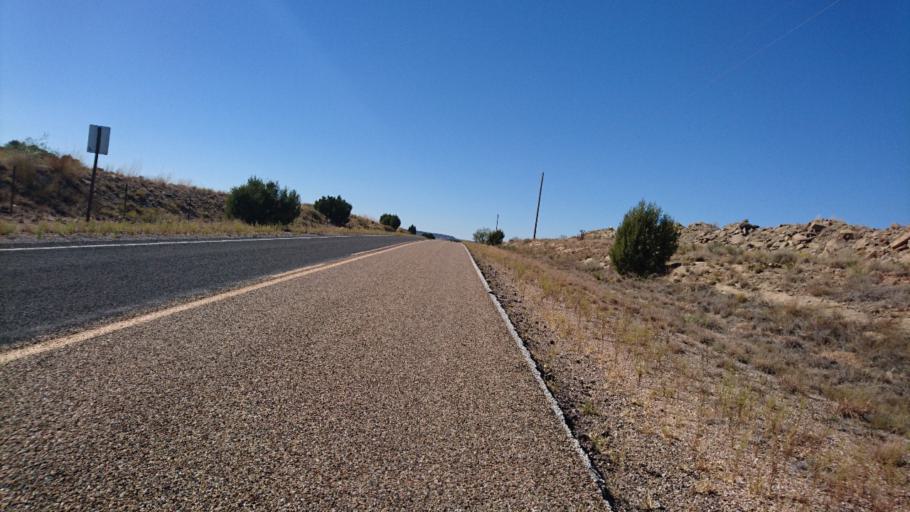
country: US
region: New Mexico
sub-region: Quay County
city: Tucumcari
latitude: 35.0683
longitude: -104.1999
